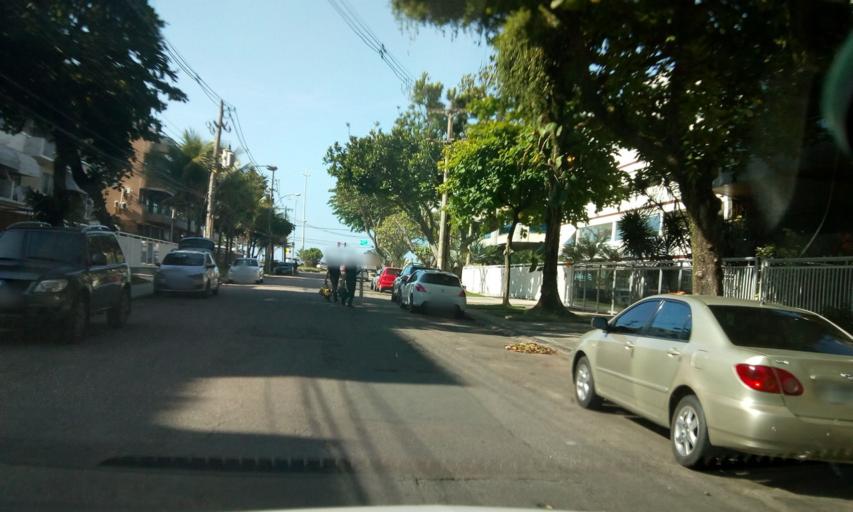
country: BR
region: Rio de Janeiro
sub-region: Rio De Janeiro
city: Rio de Janeiro
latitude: -23.0123
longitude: -43.3133
